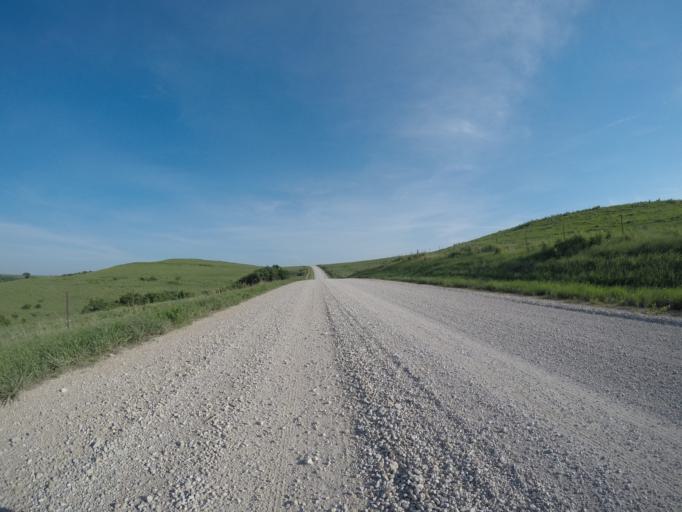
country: US
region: Kansas
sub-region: Riley County
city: Manhattan
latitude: 39.0544
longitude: -96.4962
